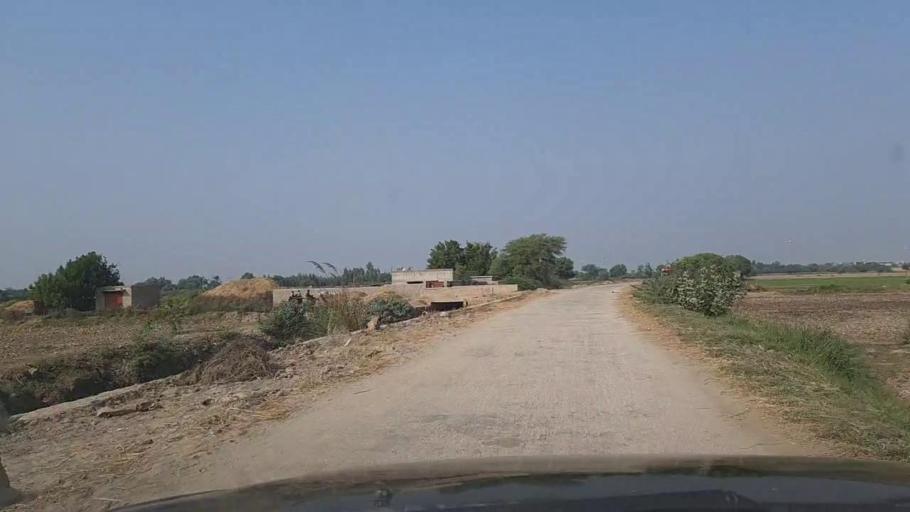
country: PK
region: Sindh
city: Mirpur Batoro
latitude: 24.7171
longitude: 68.2550
